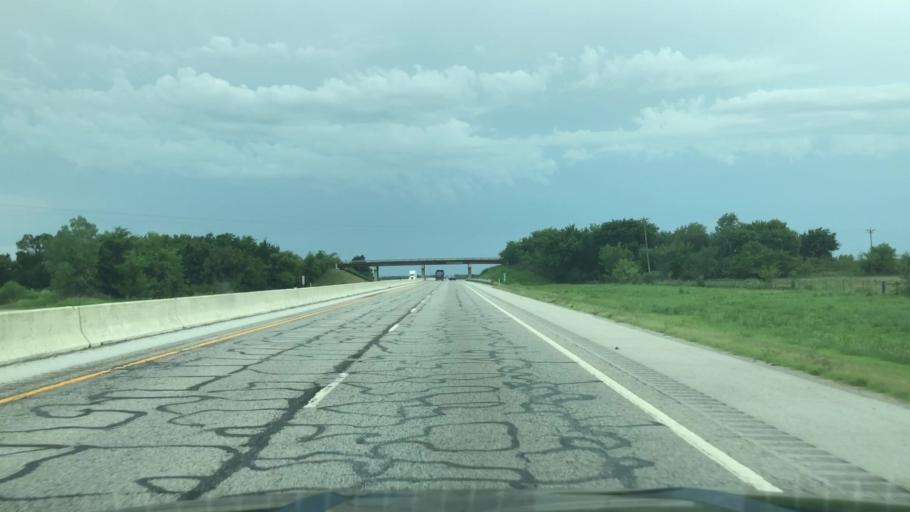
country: US
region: Oklahoma
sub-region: Craig County
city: Vinita
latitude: 36.5257
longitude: -95.2534
